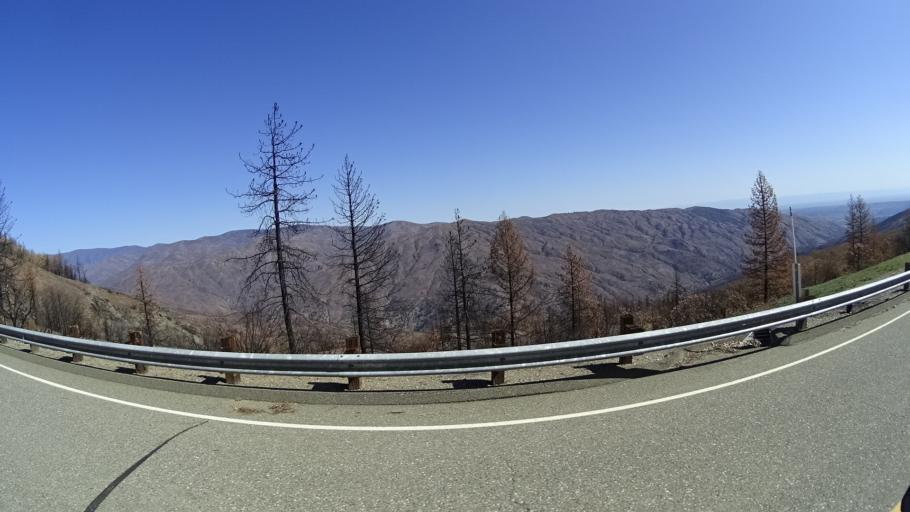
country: US
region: California
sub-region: Tehama County
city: Rancho Tehama Reserve
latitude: 39.6704
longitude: -122.6913
